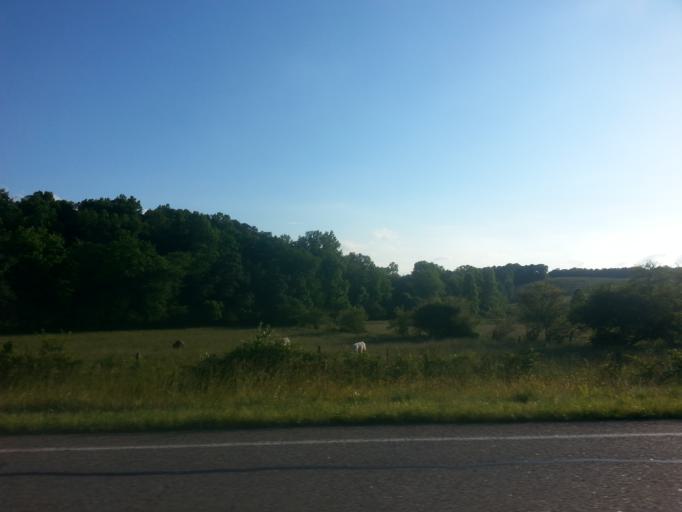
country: US
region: Georgia
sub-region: Union County
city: Blairsville
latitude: 34.9575
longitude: -84.0561
